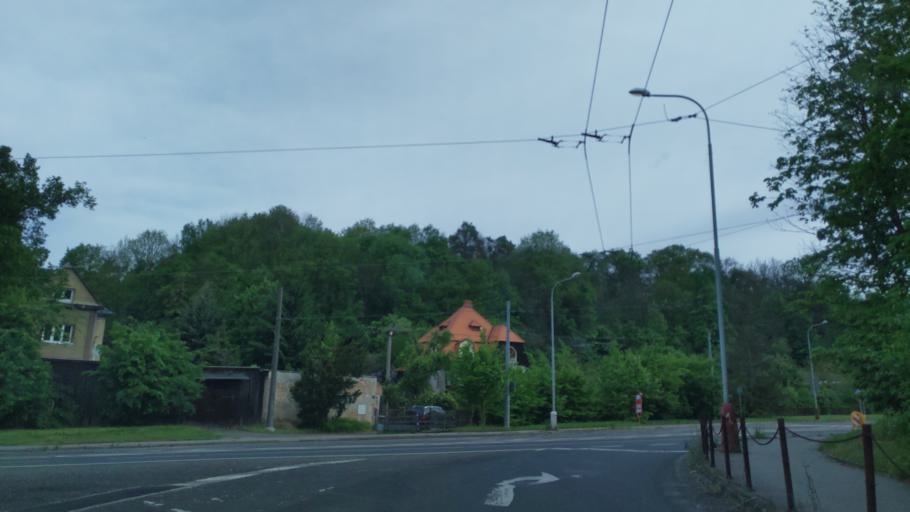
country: CZ
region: Ustecky
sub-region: Okres Usti nad Labem
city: Usti nad Labem
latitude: 50.6811
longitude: 14.0117
